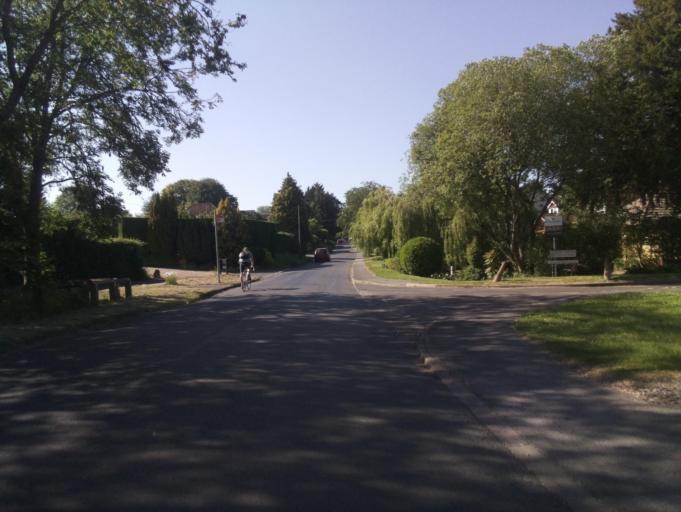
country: GB
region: England
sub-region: Hampshire
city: Winchester
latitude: 51.0862
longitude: -1.3487
